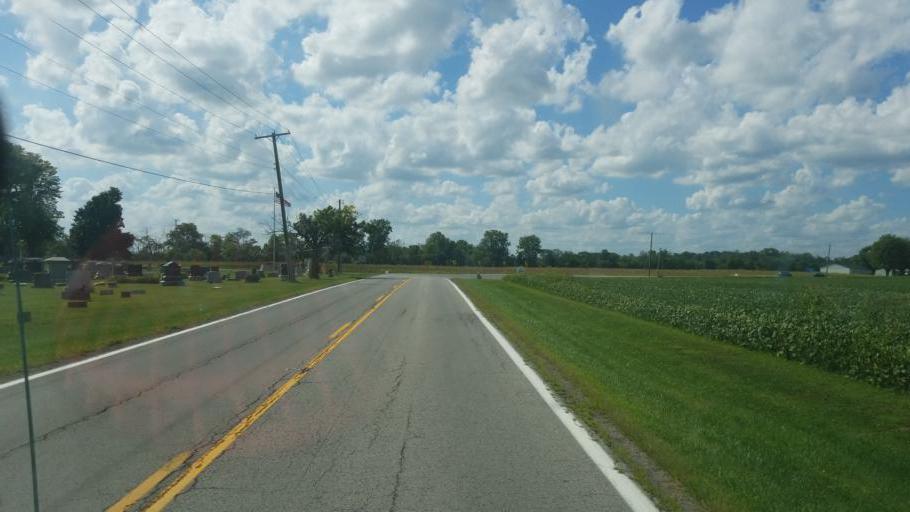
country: US
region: Ohio
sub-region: Union County
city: Richwood
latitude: 40.3965
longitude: -83.2800
